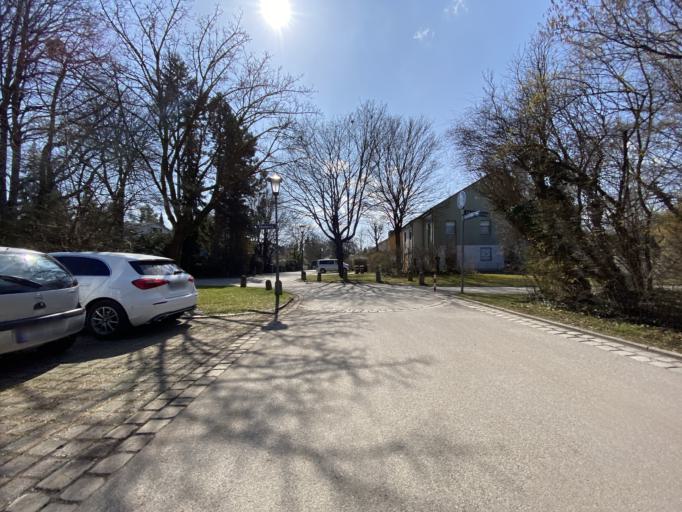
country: DE
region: Bavaria
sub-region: Upper Bavaria
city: Unterfoehring
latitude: 48.1656
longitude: 11.6590
